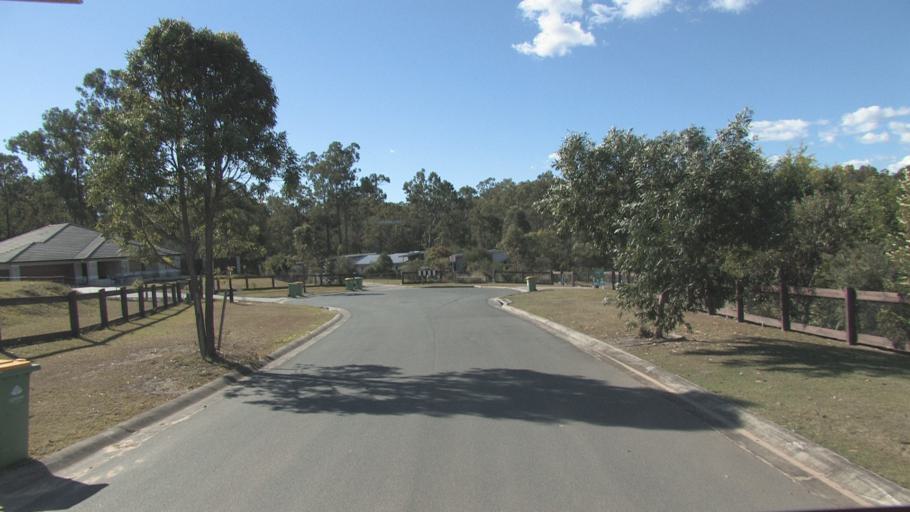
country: AU
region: Queensland
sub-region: Ipswich
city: Springfield Lakes
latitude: -27.7290
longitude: 152.9151
